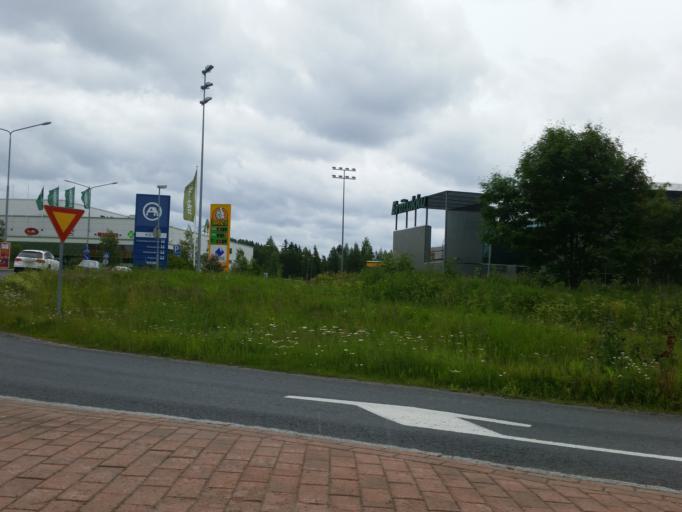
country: FI
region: Northern Savo
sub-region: Kuopio
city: Kuopio
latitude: 62.8869
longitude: 27.6295
